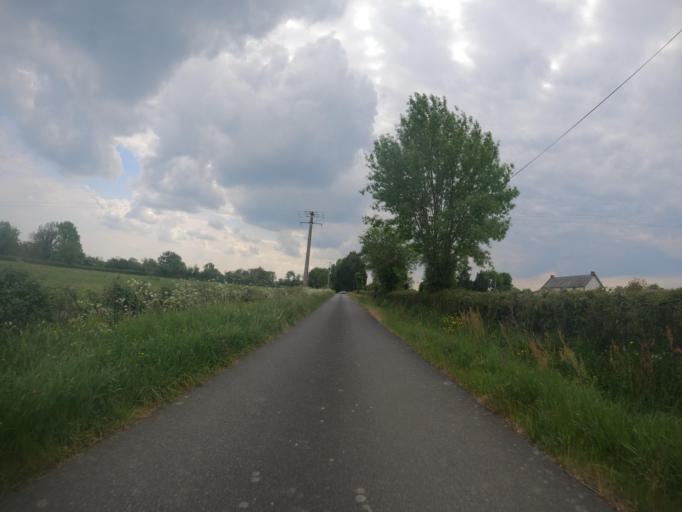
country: FR
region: Poitou-Charentes
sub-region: Departement des Deux-Sevres
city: Chiche
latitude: 46.8622
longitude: -0.3184
